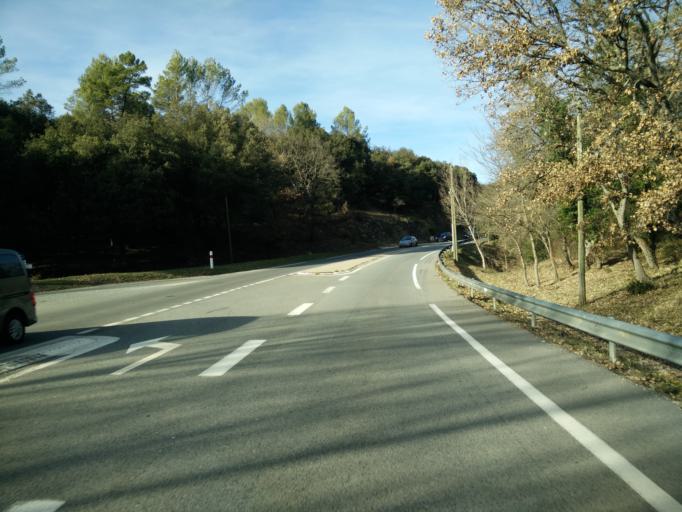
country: FR
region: Provence-Alpes-Cote d'Azur
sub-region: Departement du Var
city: Montauroux
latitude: 43.5894
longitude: 6.7899
